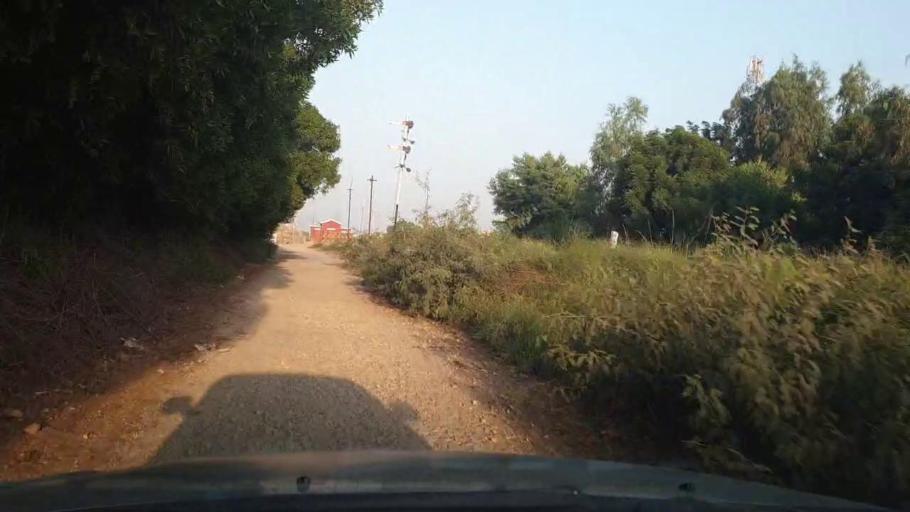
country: PK
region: Sindh
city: Tando Jam
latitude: 25.4290
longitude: 68.5233
